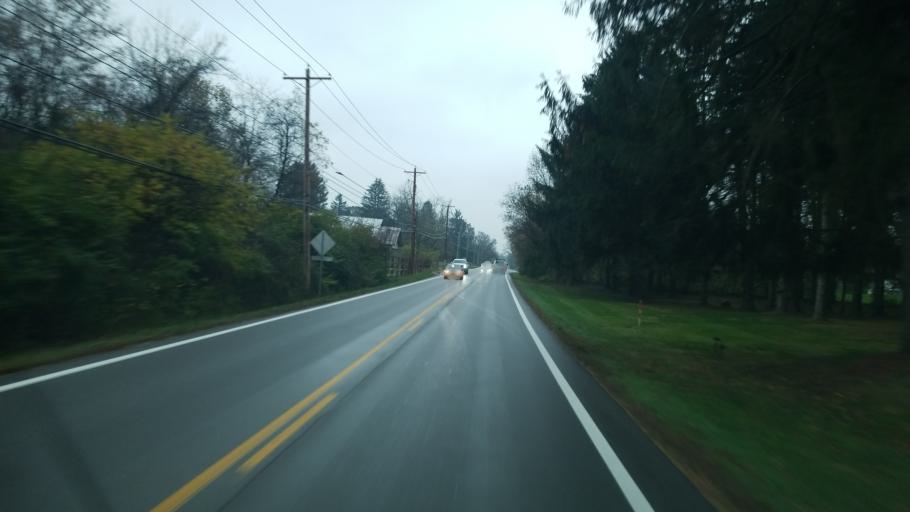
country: US
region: Ohio
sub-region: Delaware County
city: Powell
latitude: 40.1480
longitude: -83.0429
